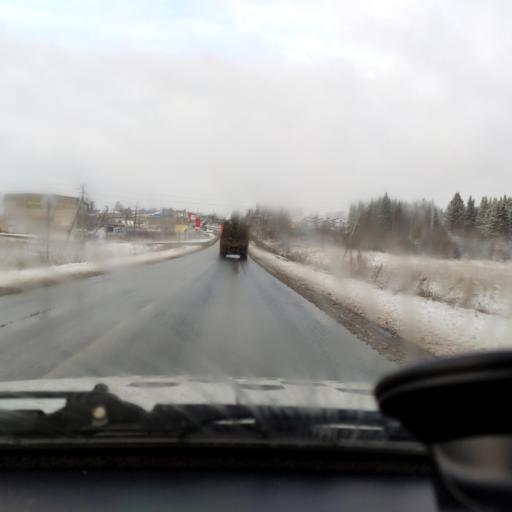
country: RU
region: Perm
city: Nytva
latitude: 57.9470
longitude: 55.3616
